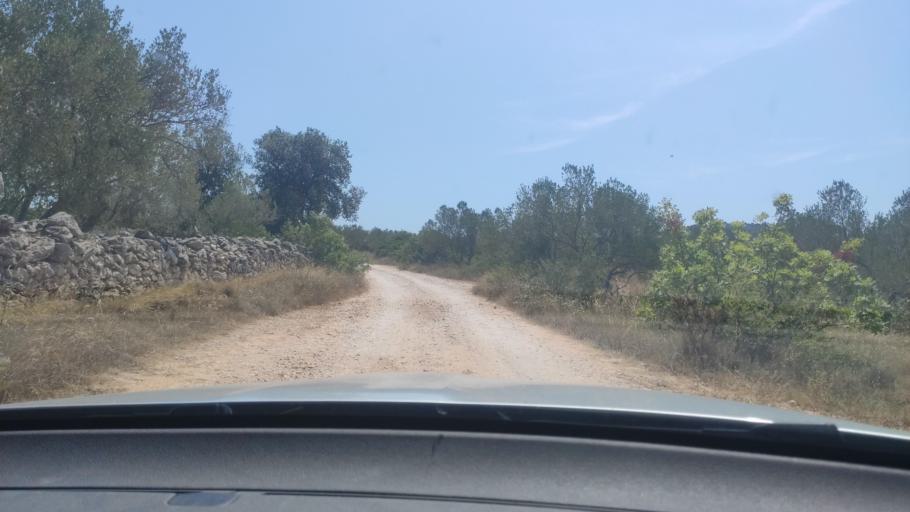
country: HR
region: Sibensko-Kniniska
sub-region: Grad Sibenik
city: Tisno
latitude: 43.7792
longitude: 15.6445
